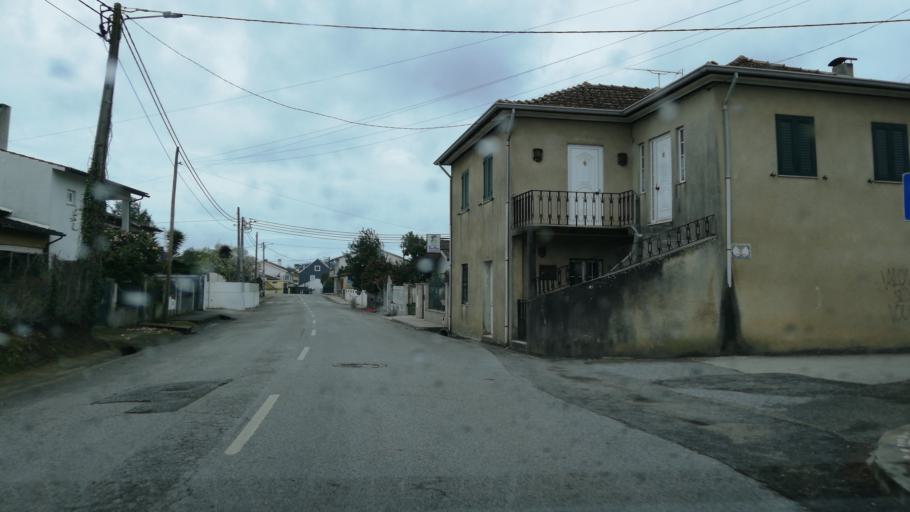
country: PT
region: Aveiro
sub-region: Agueda
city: Valongo
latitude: 40.6171
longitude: -8.4317
